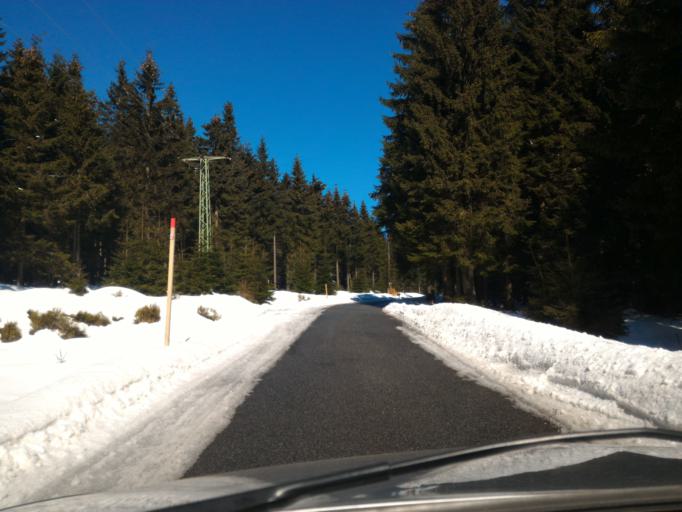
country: CZ
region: Liberecky
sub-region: Okres Jablonec nad Nisou
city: Korenov
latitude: 50.8047
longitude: 15.3522
